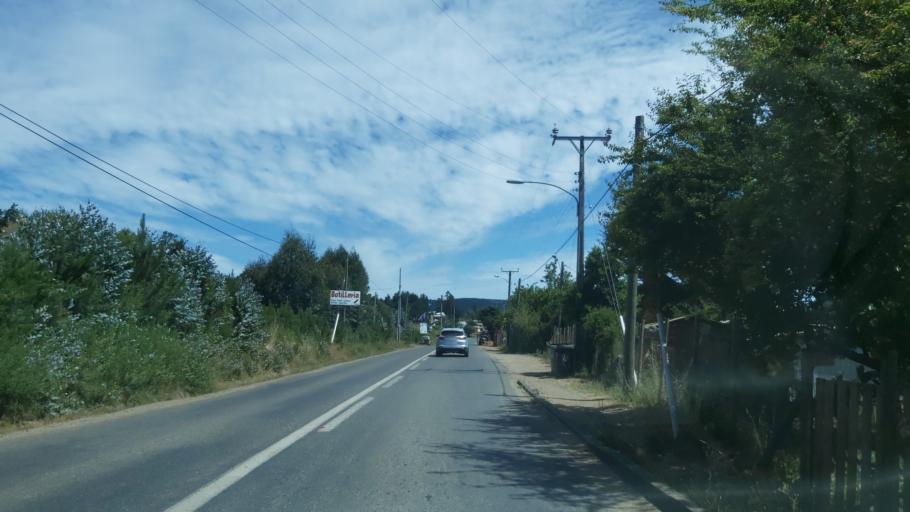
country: CL
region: Maule
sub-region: Provincia de Talca
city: Constitucion
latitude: -35.5002
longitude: -72.5183
